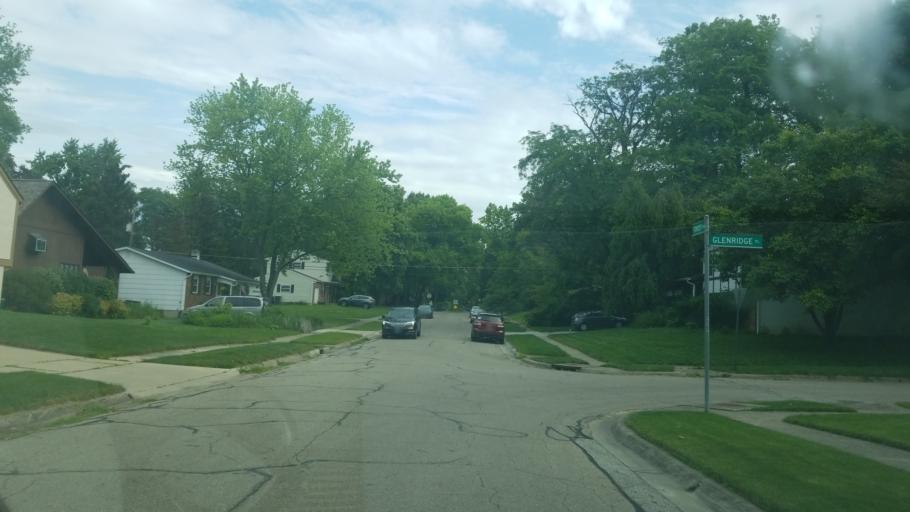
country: US
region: Ohio
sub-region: Franklin County
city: Worthington
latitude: 40.0729
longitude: -83.0044
